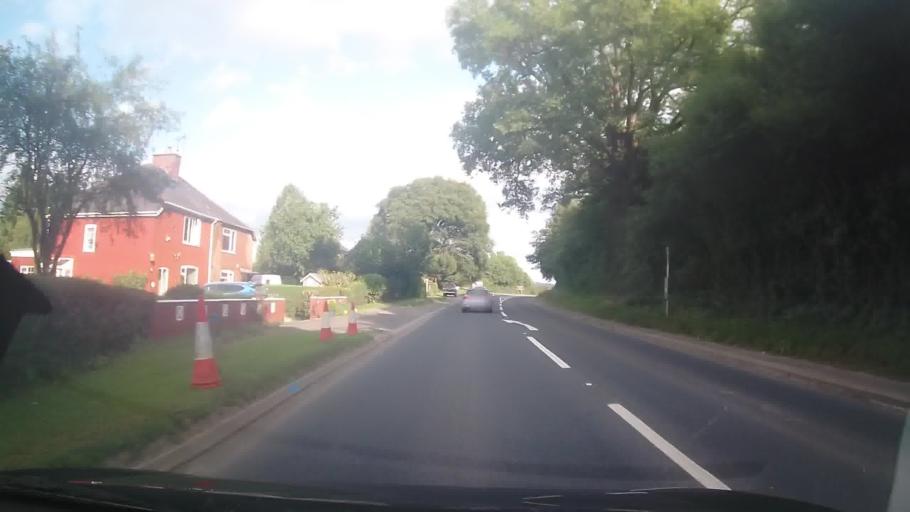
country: GB
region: England
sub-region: Shropshire
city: Bromfield
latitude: 52.3889
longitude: -2.7455
